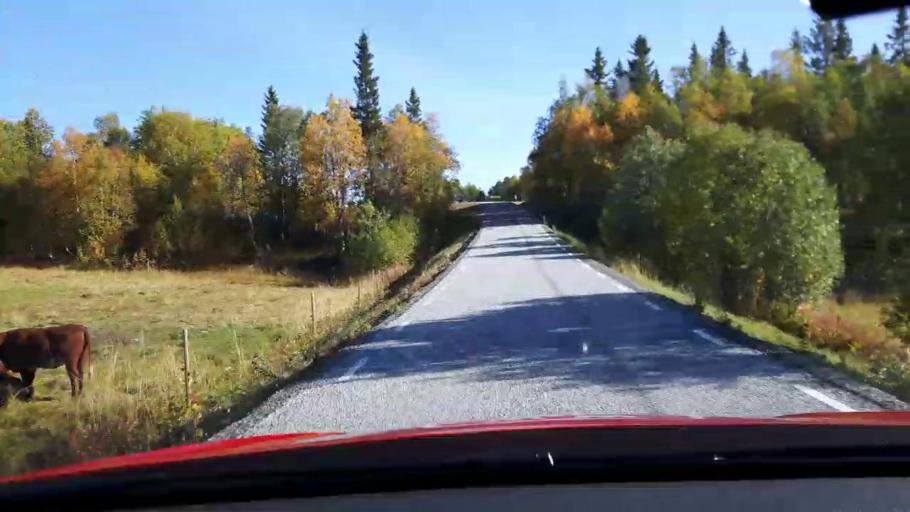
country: NO
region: Nord-Trondelag
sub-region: Royrvik
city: Royrvik
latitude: 64.8752
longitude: 14.2354
